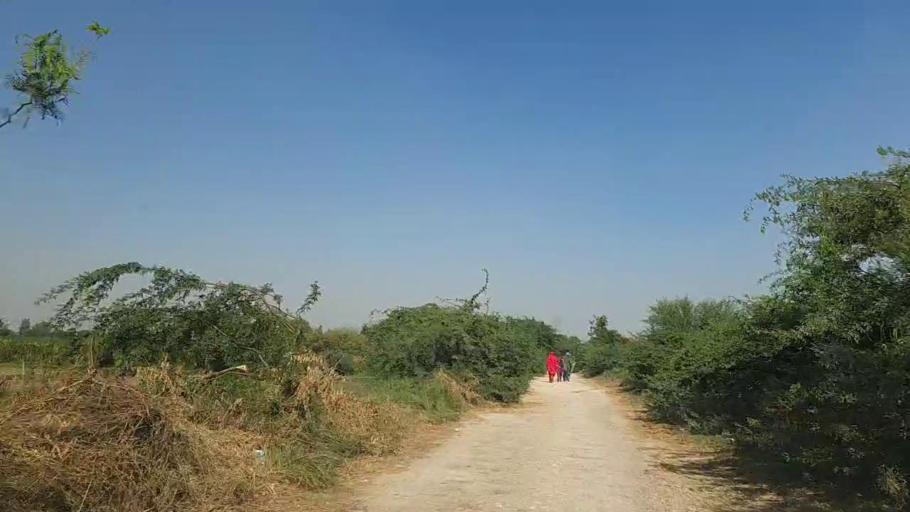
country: PK
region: Sindh
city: Daro Mehar
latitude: 24.8015
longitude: 68.1812
